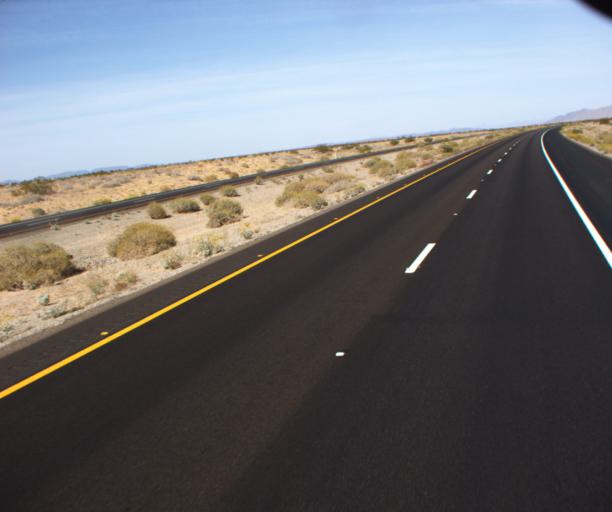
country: US
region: Arizona
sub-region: Yuma County
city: Fortuna Foothills
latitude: 32.5978
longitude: -114.5430
